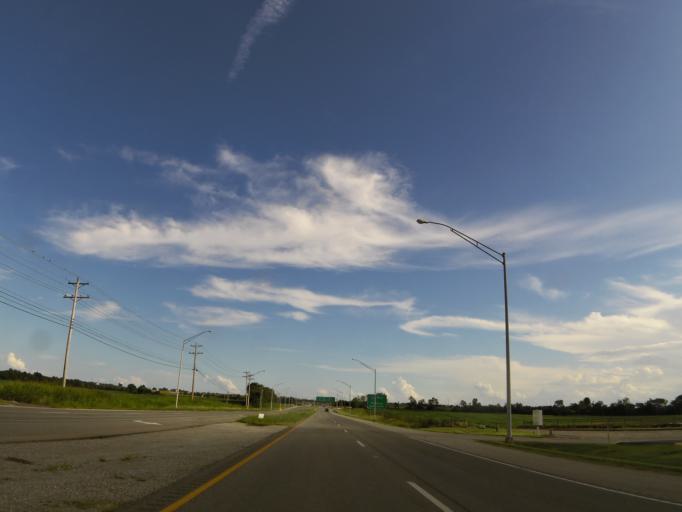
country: US
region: Kentucky
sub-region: Christian County
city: Oak Grove
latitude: 36.7098
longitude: -87.4572
